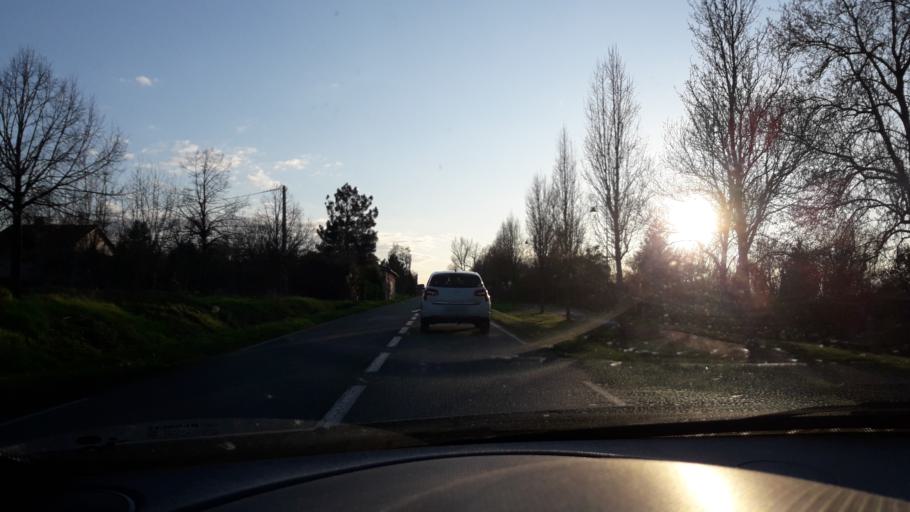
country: FR
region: Midi-Pyrenees
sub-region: Departement de la Haute-Garonne
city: Levignac
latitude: 43.6563
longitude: 1.1797
